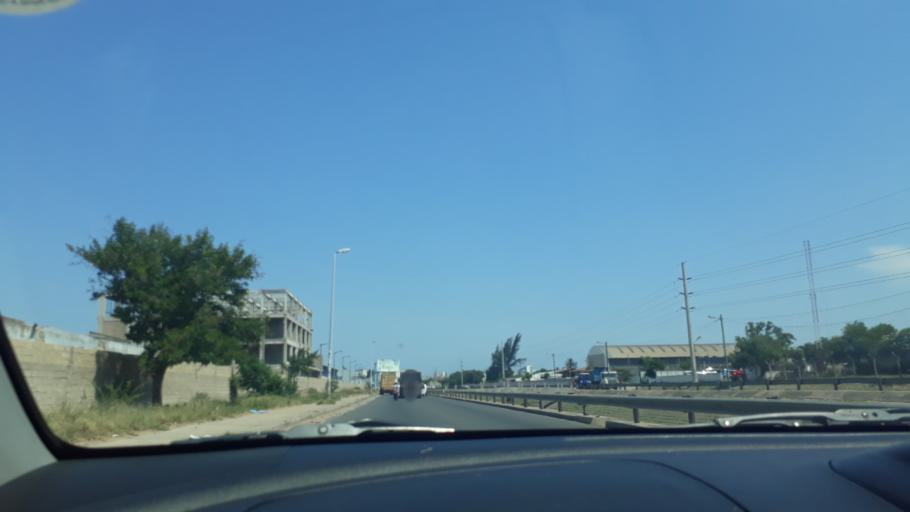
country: MZ
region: Maputo City
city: Maputo
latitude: -25.9401
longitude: 32.5692
